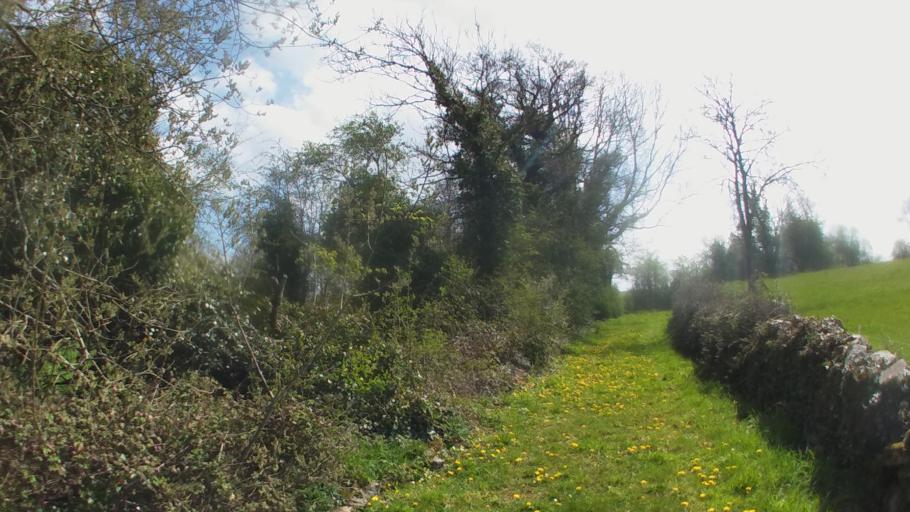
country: IE
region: Leinster
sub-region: Kilkenny
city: Thomastown
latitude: 52.5308
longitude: -7.1231
